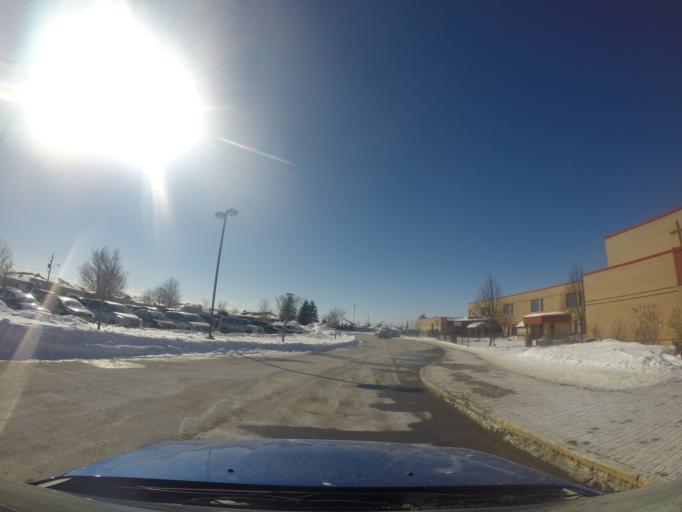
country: CA
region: Ontario
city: Omemee
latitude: 44.3401
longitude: -78.7559
